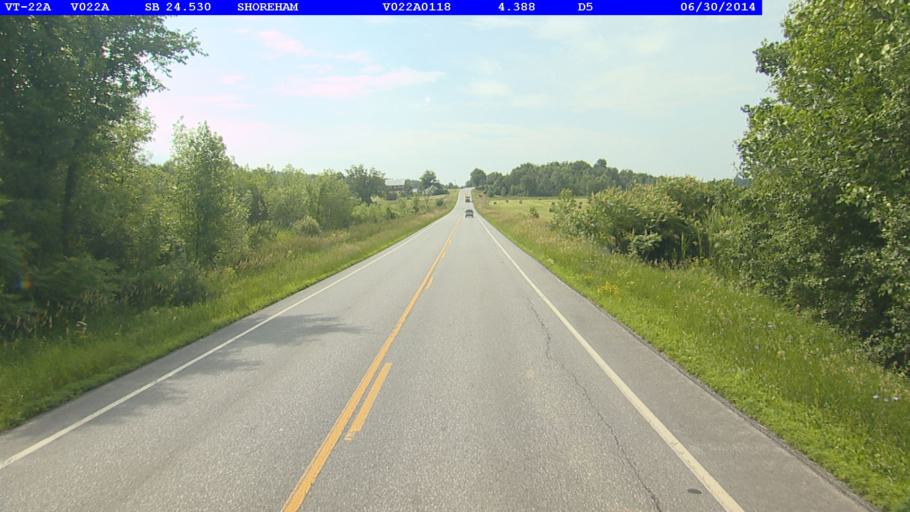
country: US
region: New York
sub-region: Essex County
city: Ticonderoga
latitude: 43.9124
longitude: -73.3114
